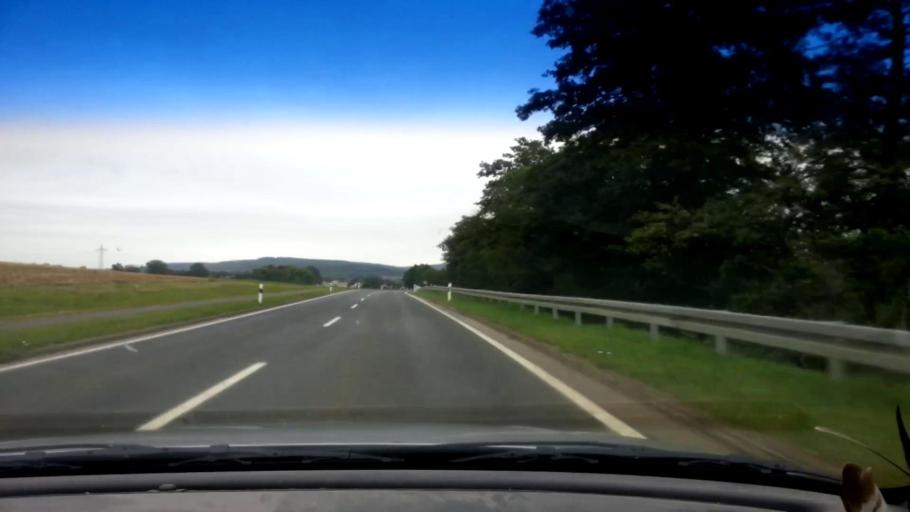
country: DE
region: Bavaria
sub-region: Upper Franconia
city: Litzendorf
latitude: 49.9154
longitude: 10.9842
